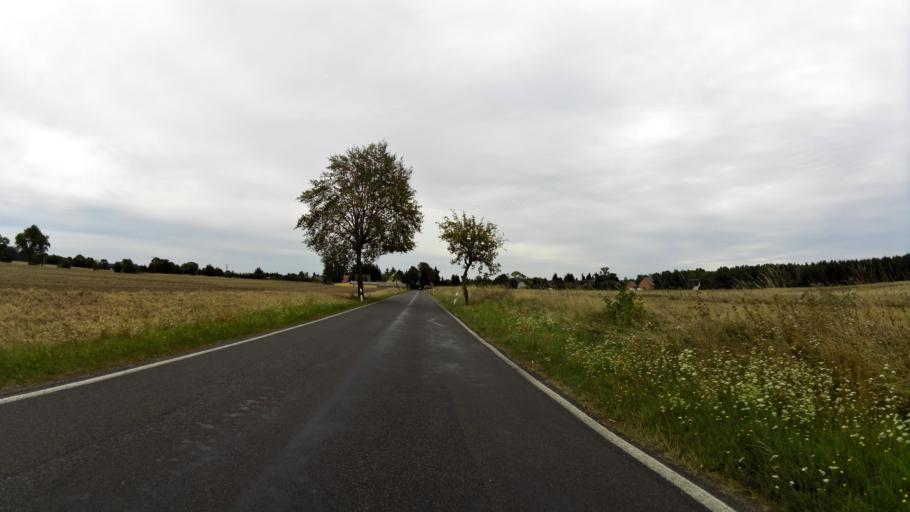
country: DE
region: Brandenburg
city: Wendisch Rietz
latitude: 52.1891
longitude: 14.0431
